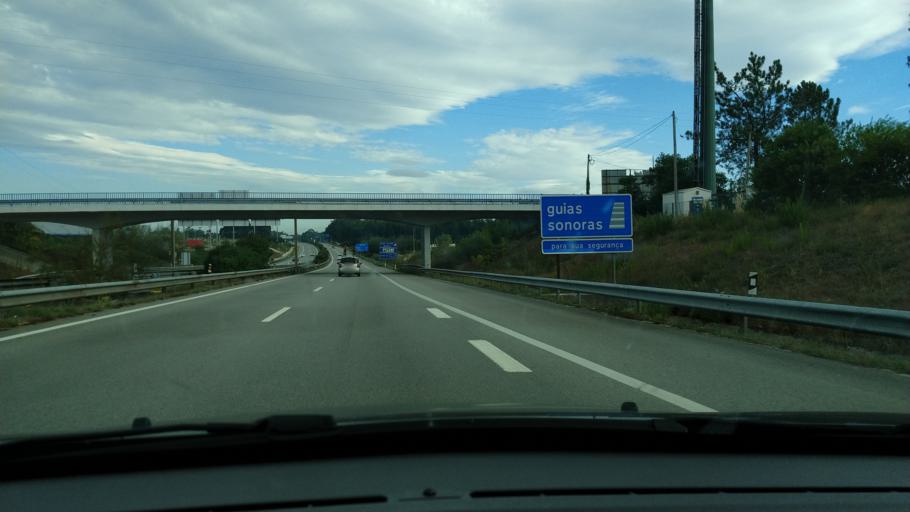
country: PT
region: Aveiro
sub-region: Aveiro
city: Eixo
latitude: 40.6518
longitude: -8.5945
